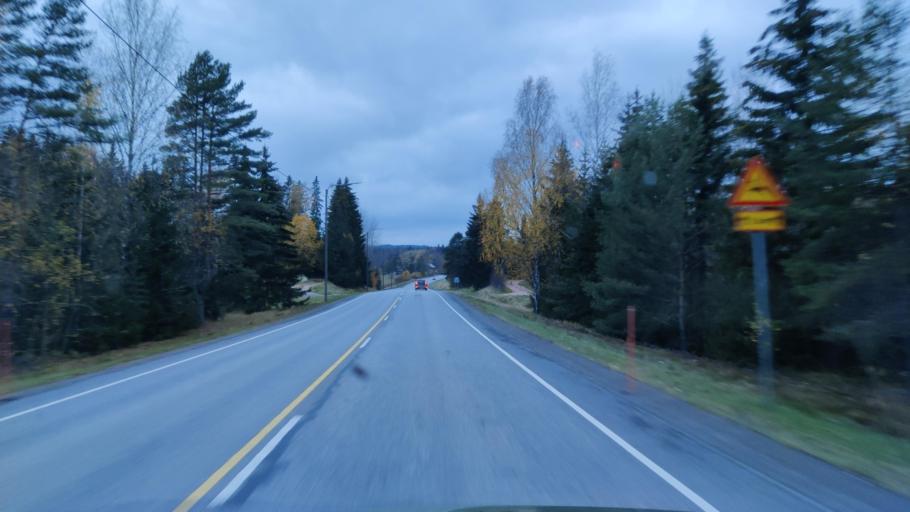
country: FI
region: Uusimaa
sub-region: Helsinki
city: Lohja
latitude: 60.3716
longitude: 24.1160
